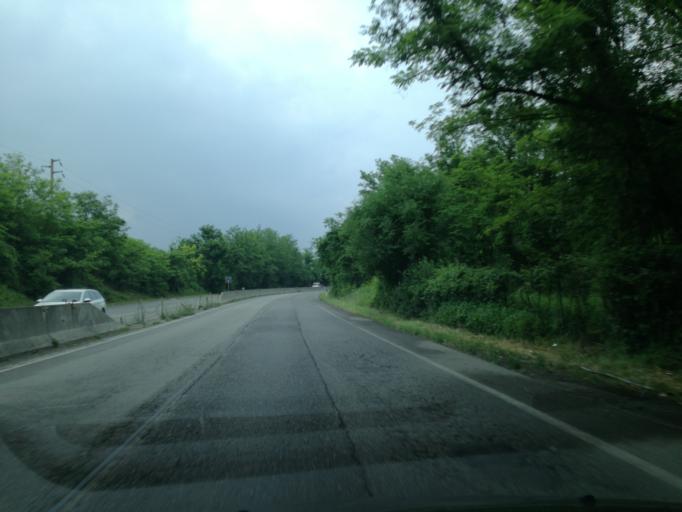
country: IT
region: Lombardy
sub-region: Provincia di Monza e Brianza
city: Villasanta
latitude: 45.6018
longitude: 9.3188
